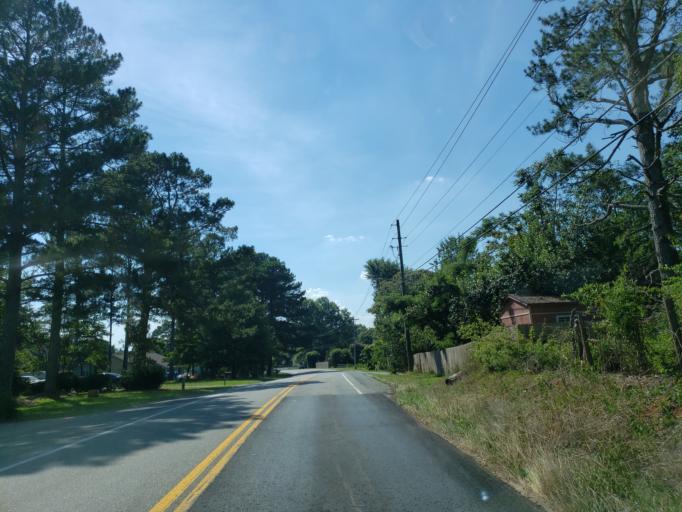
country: US
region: Georgia
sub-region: Cherokee County
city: Woodstock
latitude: 34.1173
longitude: -84.4643
